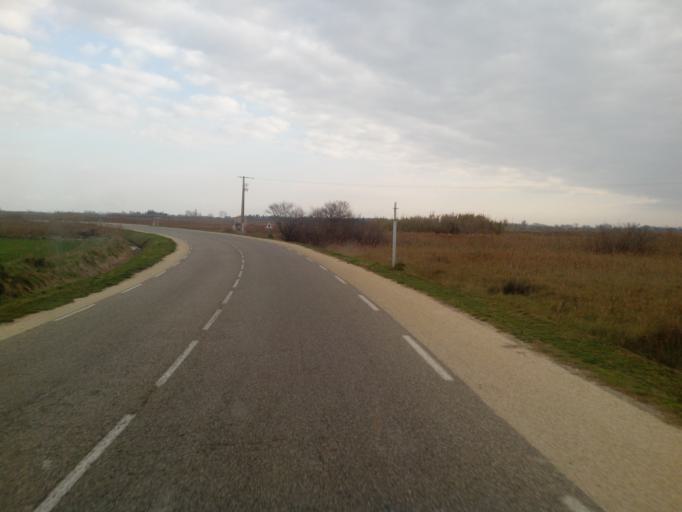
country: FR
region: Provence-Alpes-Cote d'Azur
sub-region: Departement des Bouches-du-Rhone
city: Saintes-Maries-de-la-Mer
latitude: 43.5449
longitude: 4.3528
